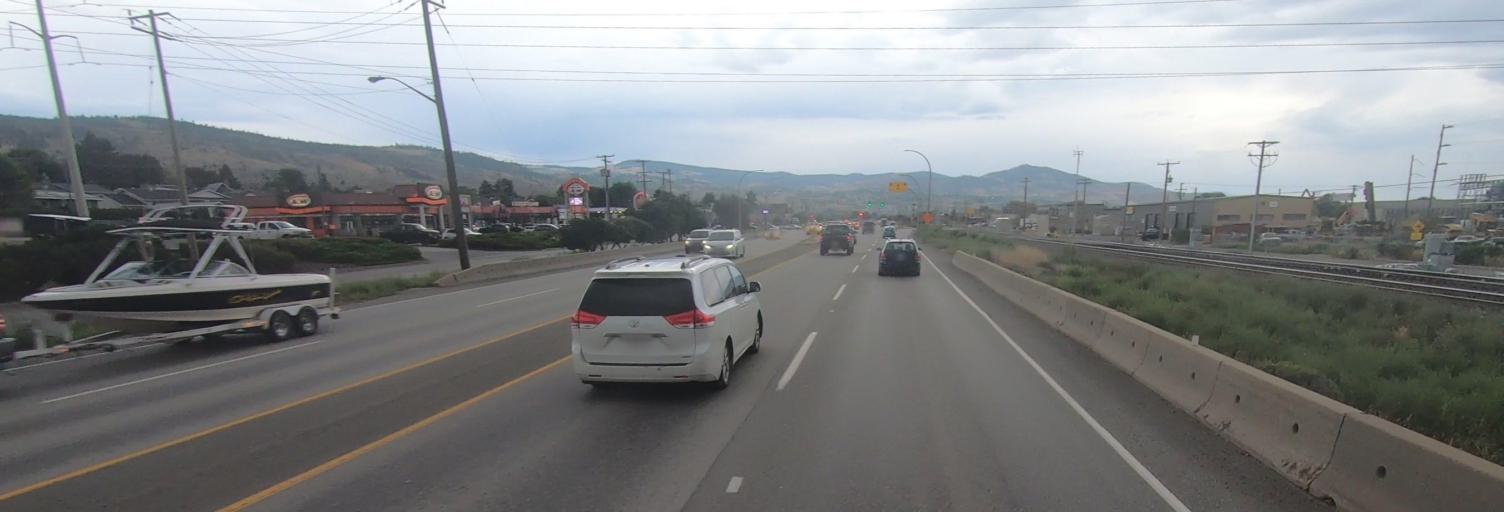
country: CA
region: British Columbia
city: Kamloops
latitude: 50.6792
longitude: -120.2803
